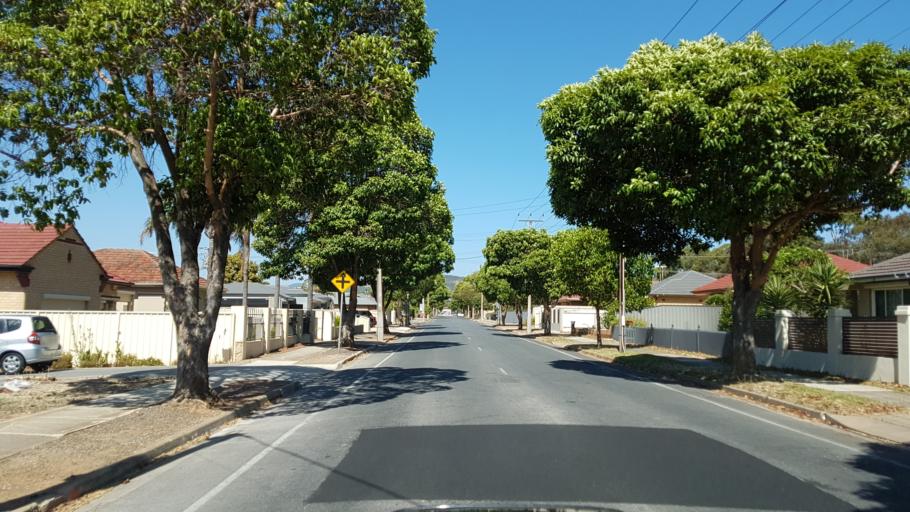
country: AU
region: South Australia
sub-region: Marion
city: Clovelly Park
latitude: -35.0001
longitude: 138.5682
